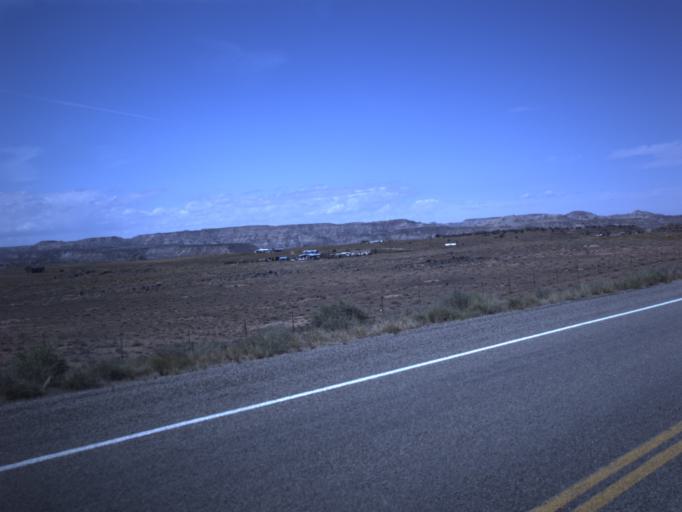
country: US
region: Colorado
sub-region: Montezuma County
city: Towaoc
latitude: 37.1763
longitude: -109.1130
